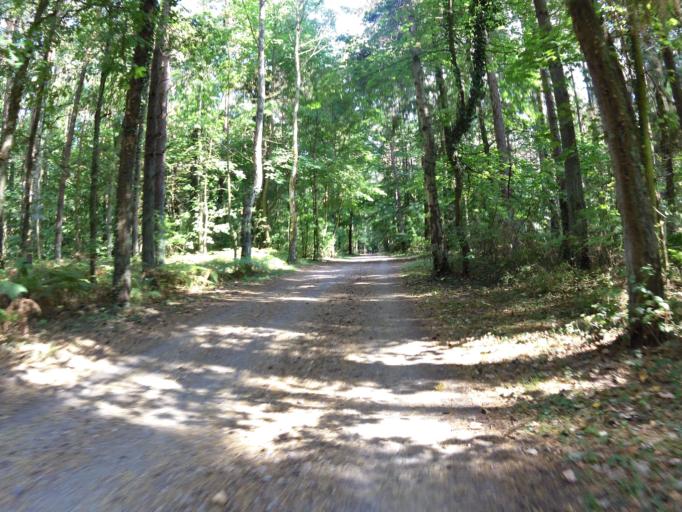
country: DE
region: Mecklenburg-Vorpommern
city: Ostseebad Zinnowitz
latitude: 54.0730
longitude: 13.9311
